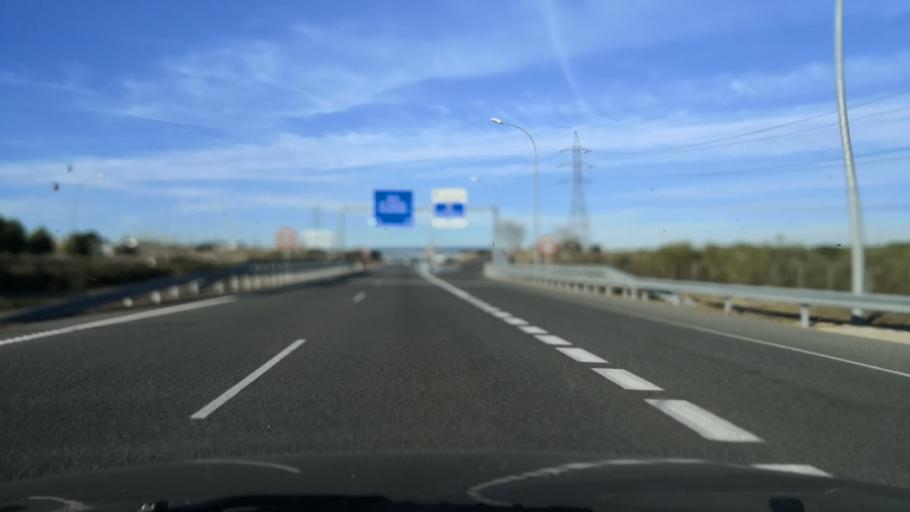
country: ES
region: Madrid
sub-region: Provincia de Madrid
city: San Sebastian de los Reyes
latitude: 40.5203
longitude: -3.5997
